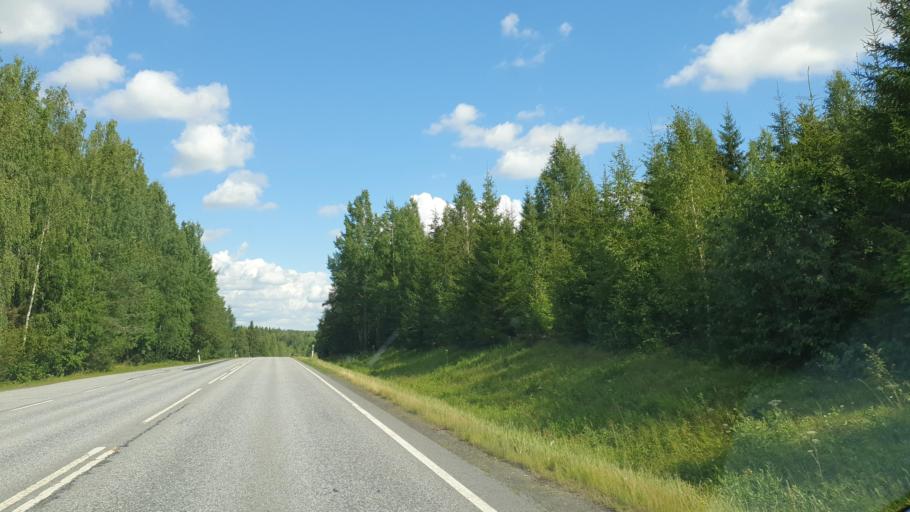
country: FI
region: Northern Savo
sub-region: Ylae-Savo
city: Sonkajaervi
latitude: 63.7520
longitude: 27.3875
